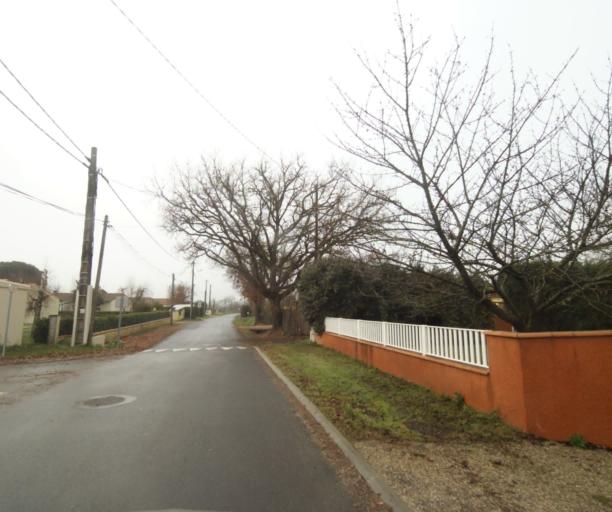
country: FR
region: Midi-Pyrenees
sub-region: Departement du Tarn-et-Garonne
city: Nohic
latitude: 43.8758
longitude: 1.4628
